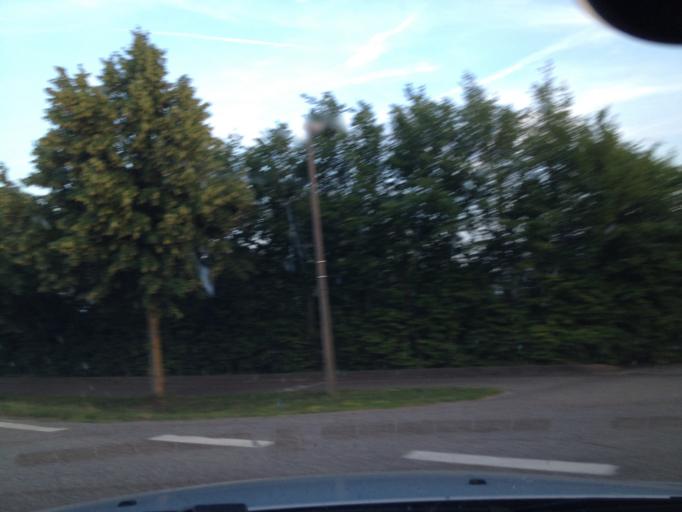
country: DE
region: Bavaria
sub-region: Regierungsbezirk Mittelfranken
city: Schillingsfurst
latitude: 49.2579
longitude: 10.2337
